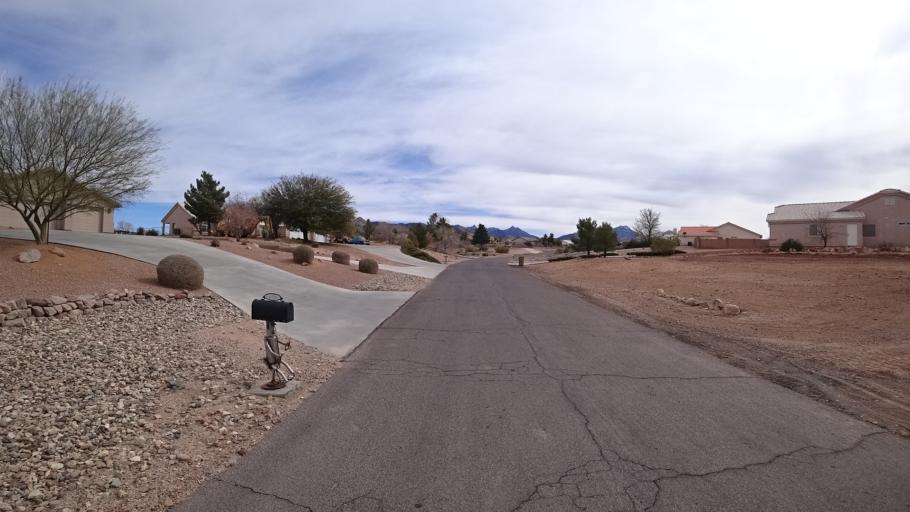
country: US
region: Arizona
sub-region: Mohave County
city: Kingman
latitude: 35.1850
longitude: -113.9816
